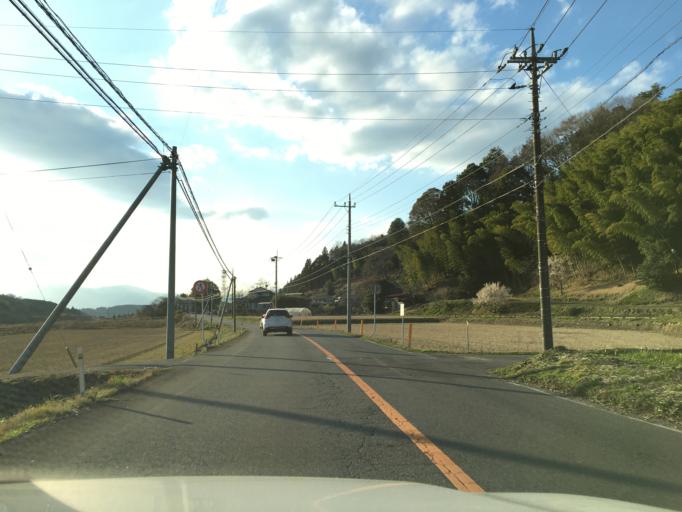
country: JP
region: Tochigi
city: Otawara
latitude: 36.8669
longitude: 140.1588
